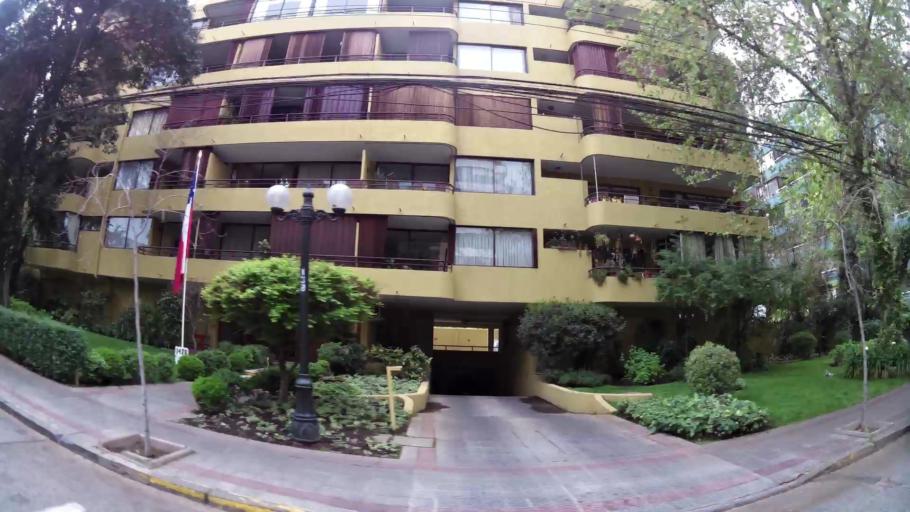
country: CL
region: Santiago Metropolitan
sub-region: Provincia de Santiago
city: Villa Presidente Frei, Nunoa, Santiago, Chile
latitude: -33.4308
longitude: -70.5983
